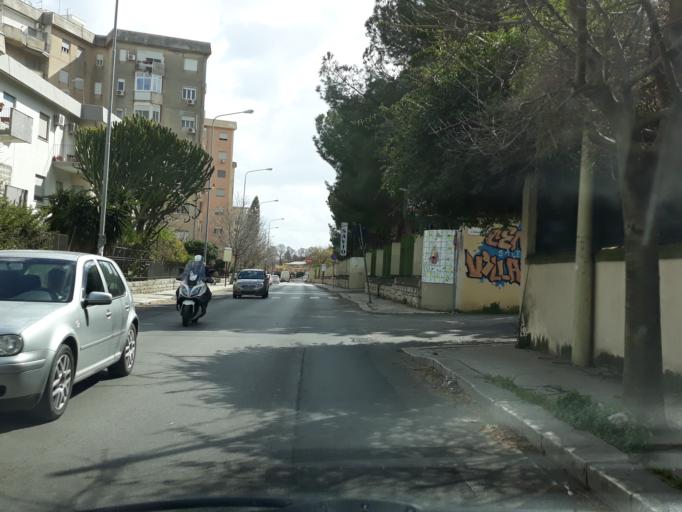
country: IT
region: Sicily
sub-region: Palermo
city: Palermo
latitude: 38.1237
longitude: 13.3187
